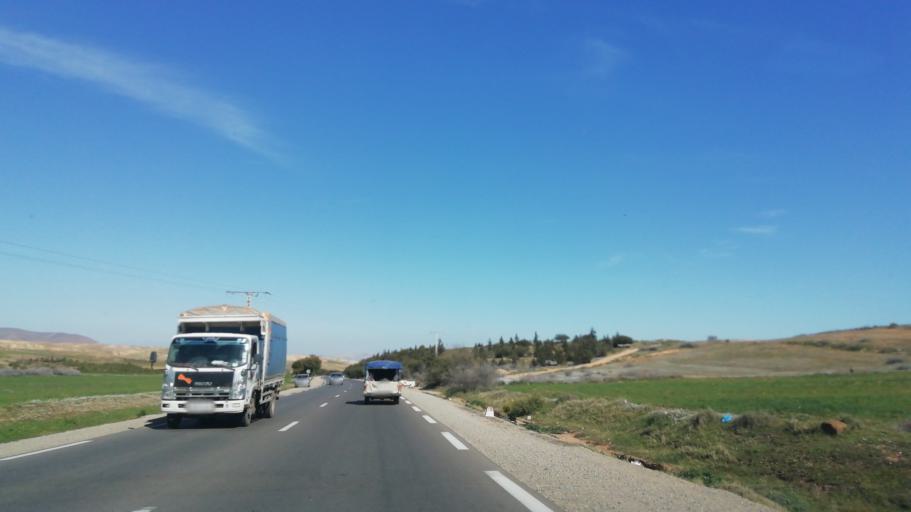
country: DZ
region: Mascara
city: Oued el Abtal
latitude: 35.4338
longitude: 0.4920
